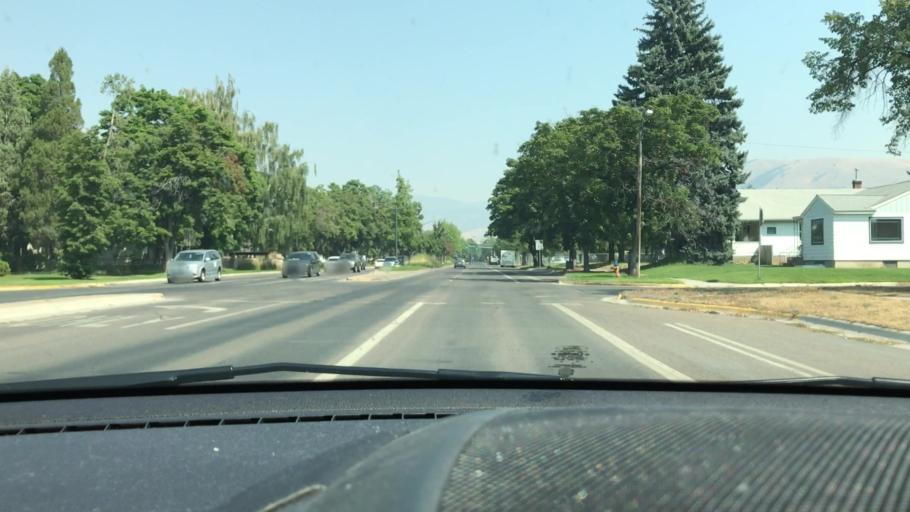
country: US
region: Montana
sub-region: Missoula County
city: Missoula
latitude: 46.8597
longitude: -114.0083
